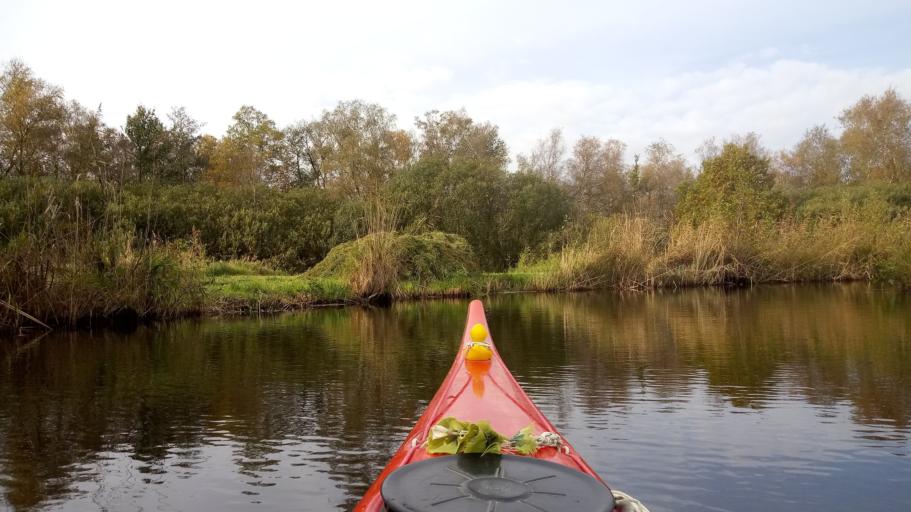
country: NL
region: Overijssel
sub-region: Gemeente Steenwijkerland
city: Sint Jansklooster
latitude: 52.6666
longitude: 6.0386
